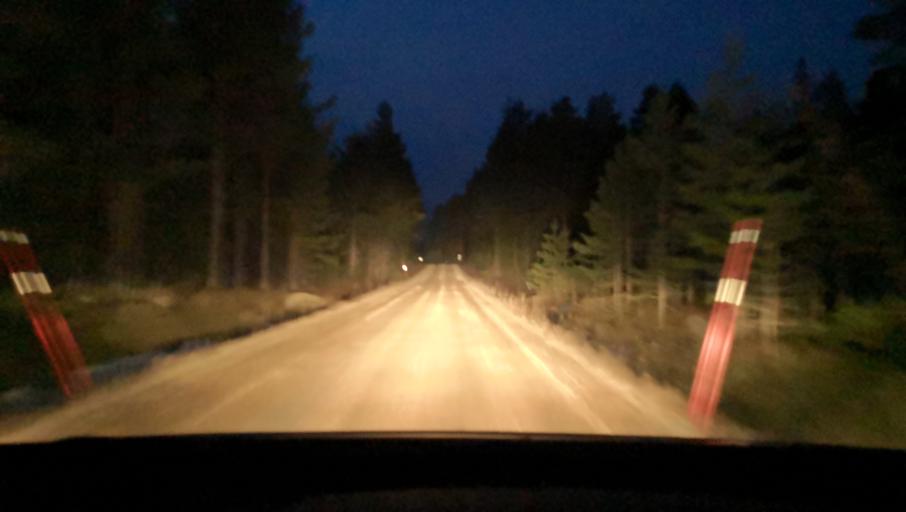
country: SE
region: OErebro
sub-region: Lindesbergs Kommun
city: Frovi
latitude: 59.6635
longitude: 15.5037
